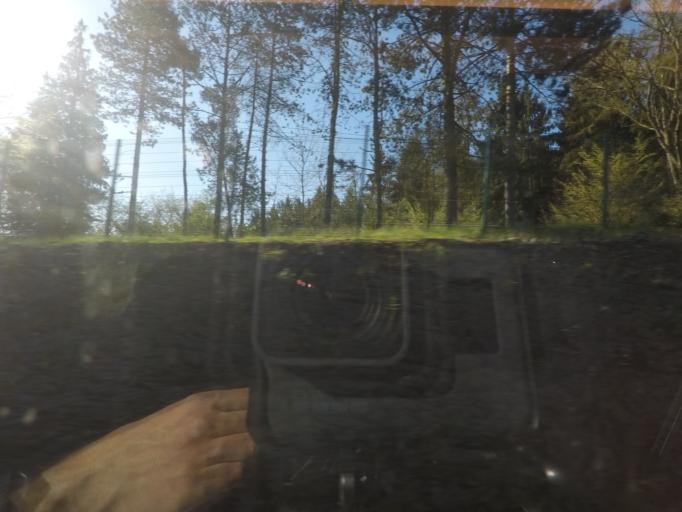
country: BE
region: Wallonia
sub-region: Province de Namur
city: Rochefort
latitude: 50.2472
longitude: 5.2326
